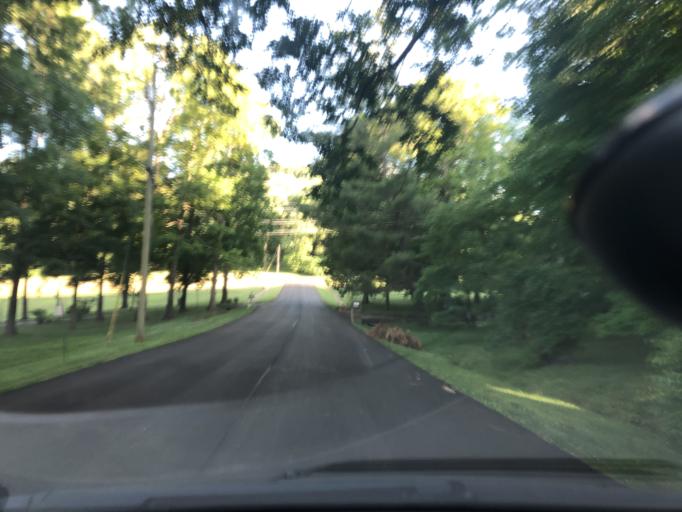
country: US
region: Tennessee
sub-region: Davidson County
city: Forest Hills
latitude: 36.0566
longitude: -86.8373
